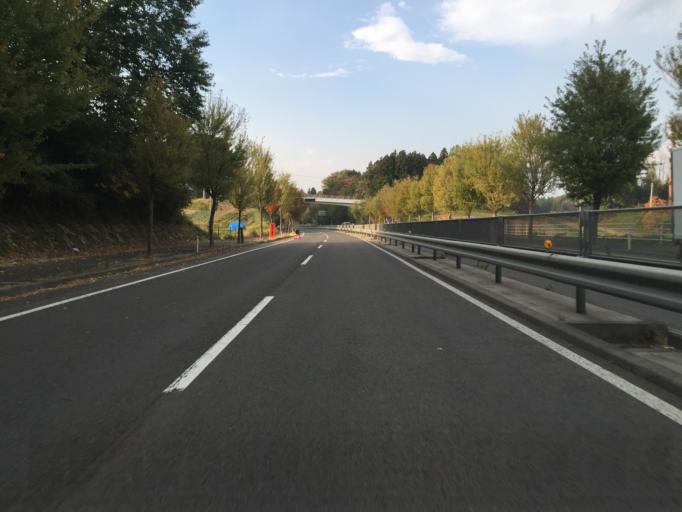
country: JP
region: Fukushima
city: Fukushima-shi
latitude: 37.6645
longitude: 140.4890
